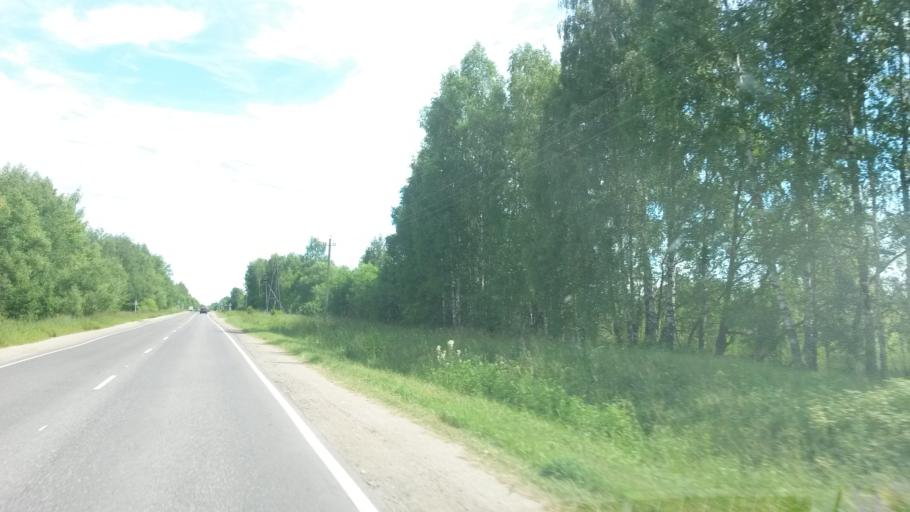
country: RU
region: Ivanovo
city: Zavolzhsk
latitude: 57.5062
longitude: 42.0975
